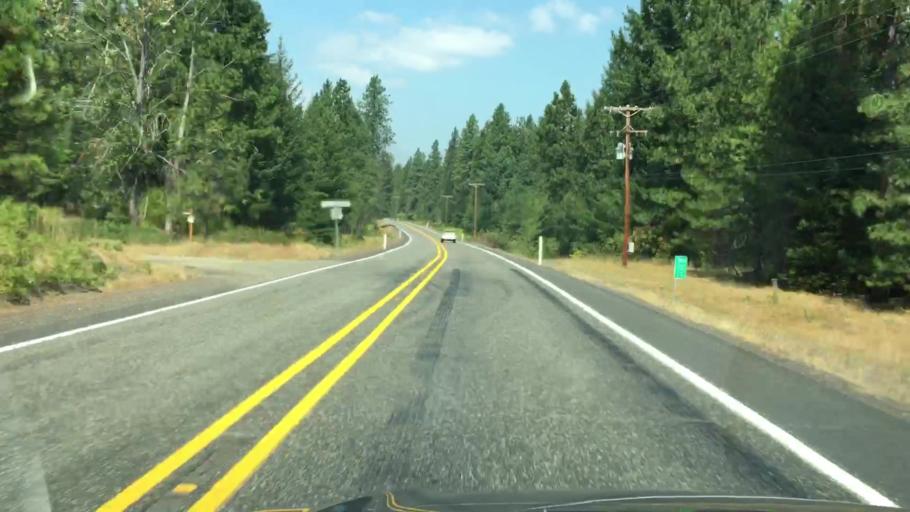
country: US
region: Washington
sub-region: Klickitat County
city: White Salmon
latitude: 45.9644
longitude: -121.4905
